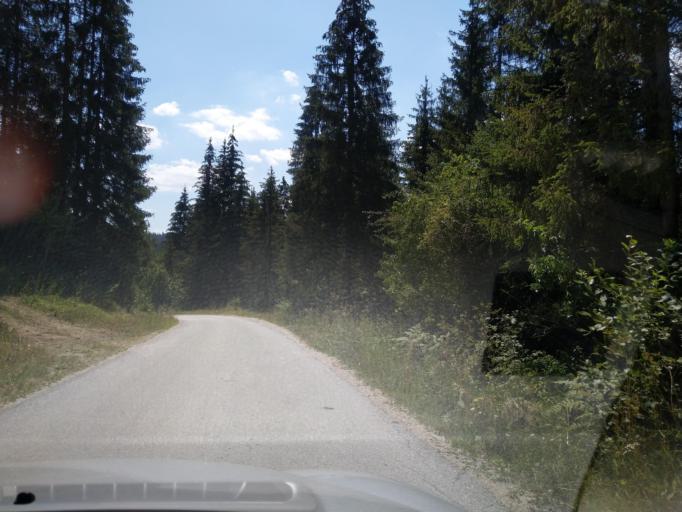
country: RS
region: Central Serbia
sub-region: Zlatiborski Okrug
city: Nova Varos
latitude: 43.4770
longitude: 19.9654
